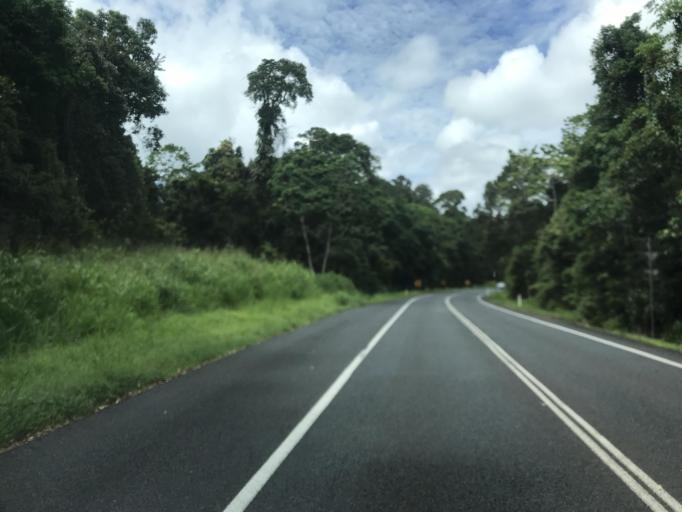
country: AU
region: Queensland
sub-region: Tablelands
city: Ravenshoe
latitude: -17.5927
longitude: 145.7360
